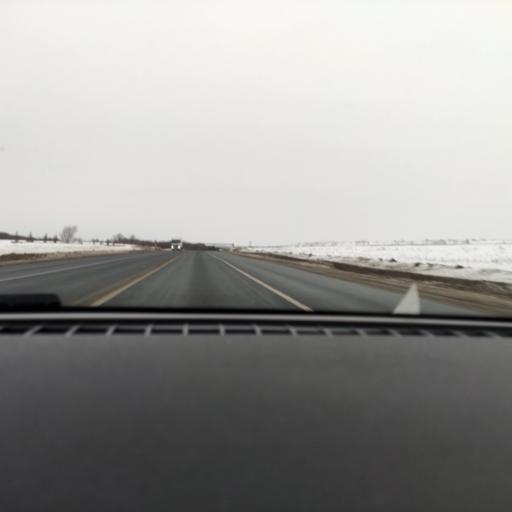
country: RU
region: Samara
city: Petra-Dubrava
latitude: 53.3409
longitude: 50.4516
